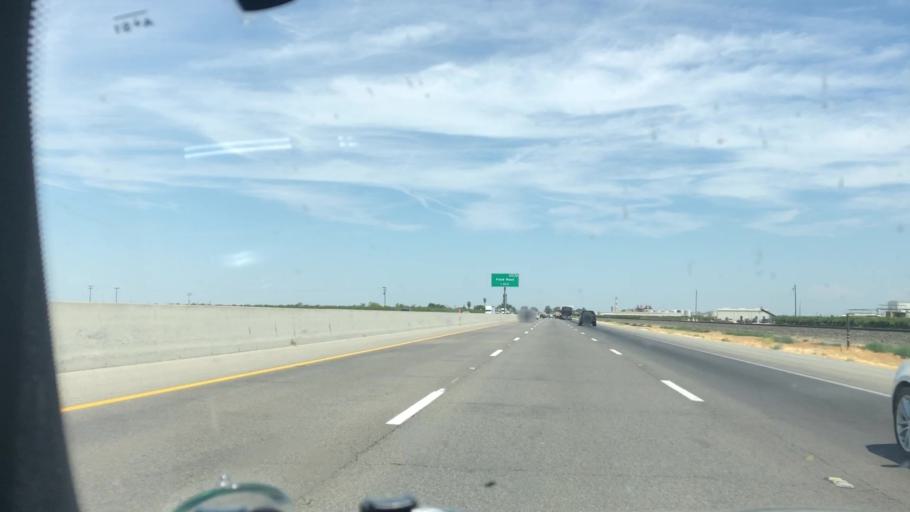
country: US
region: California
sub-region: Kern County
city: McFarland
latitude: 35.7009
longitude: -119.2324
